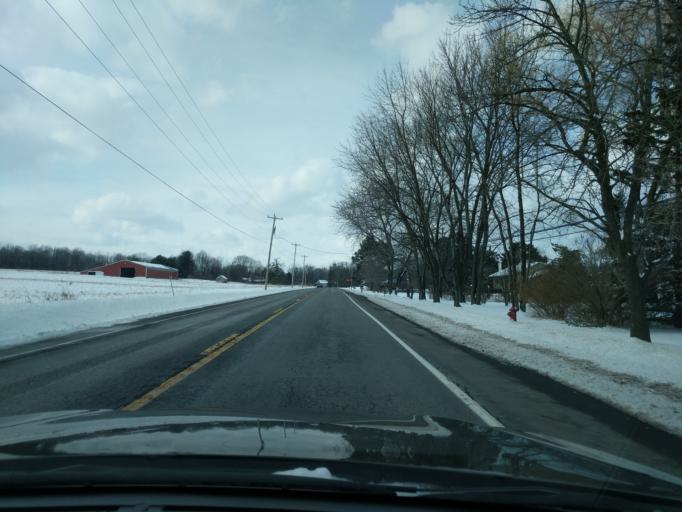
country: US
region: New York
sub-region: Tompkins County
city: Northwest Ithaca
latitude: 42.4837
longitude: -76.5675
